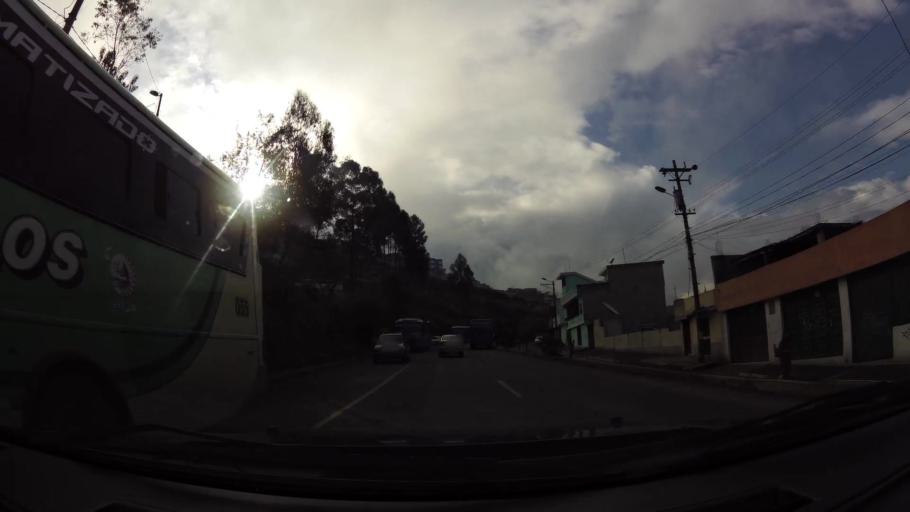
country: EC
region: Pichincha
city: Quito
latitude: -0.2472
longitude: -78.4959
